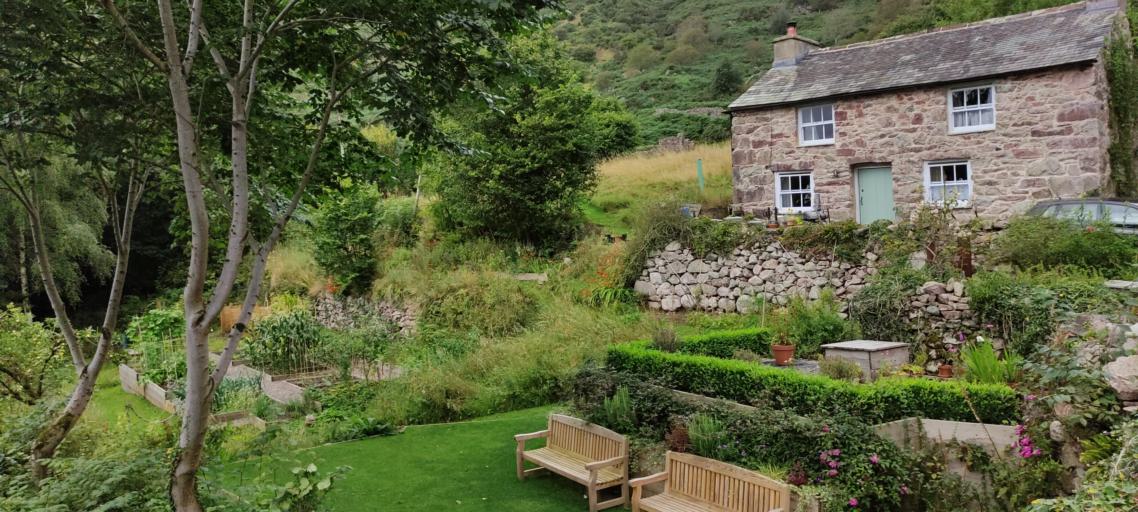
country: GB
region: England
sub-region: Cumbria
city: Millom
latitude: 54.3989
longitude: -3.2702
